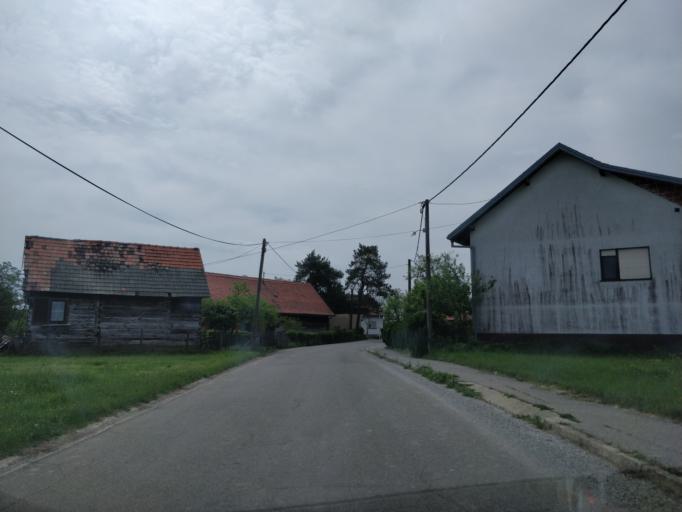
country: HR
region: Zagrebacka
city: Mraclin
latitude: 45.6214
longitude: 16.0423
